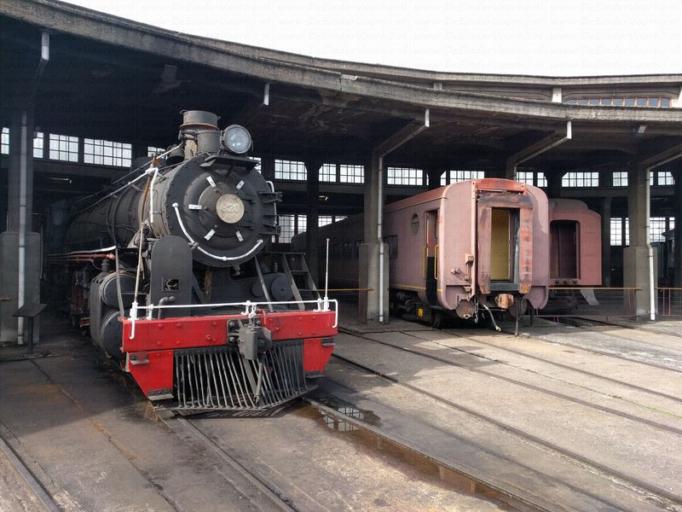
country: CL
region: Araucania
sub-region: Provincia de Cautin
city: Temuco
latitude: -38.7258
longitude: -72.5709
